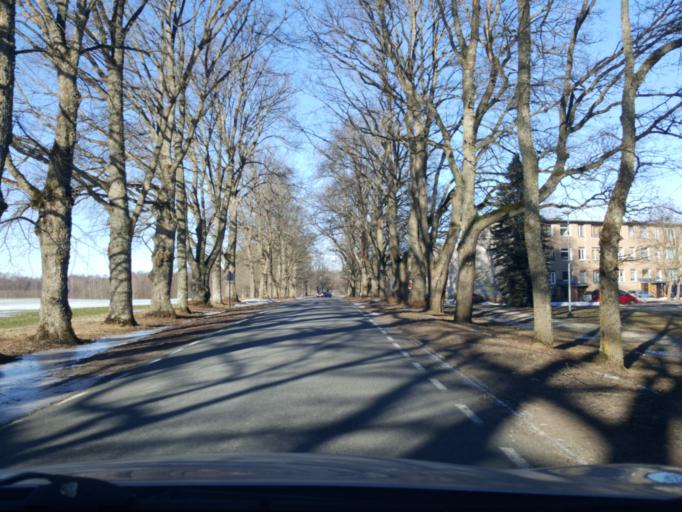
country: EE
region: Viljandimaa
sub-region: Vohma linn
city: Vohma
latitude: 58.5545
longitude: 25.5599
